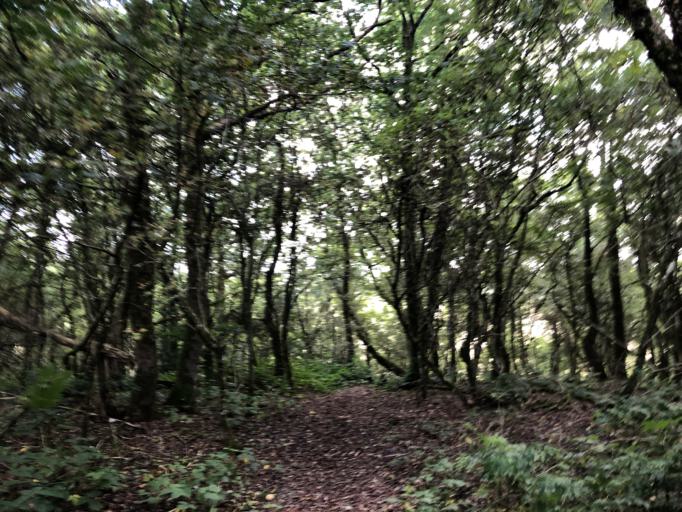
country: DK
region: Central Jutland
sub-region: Holstebro Kommune
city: Ulfborg
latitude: 56.3831
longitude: 8.3595
